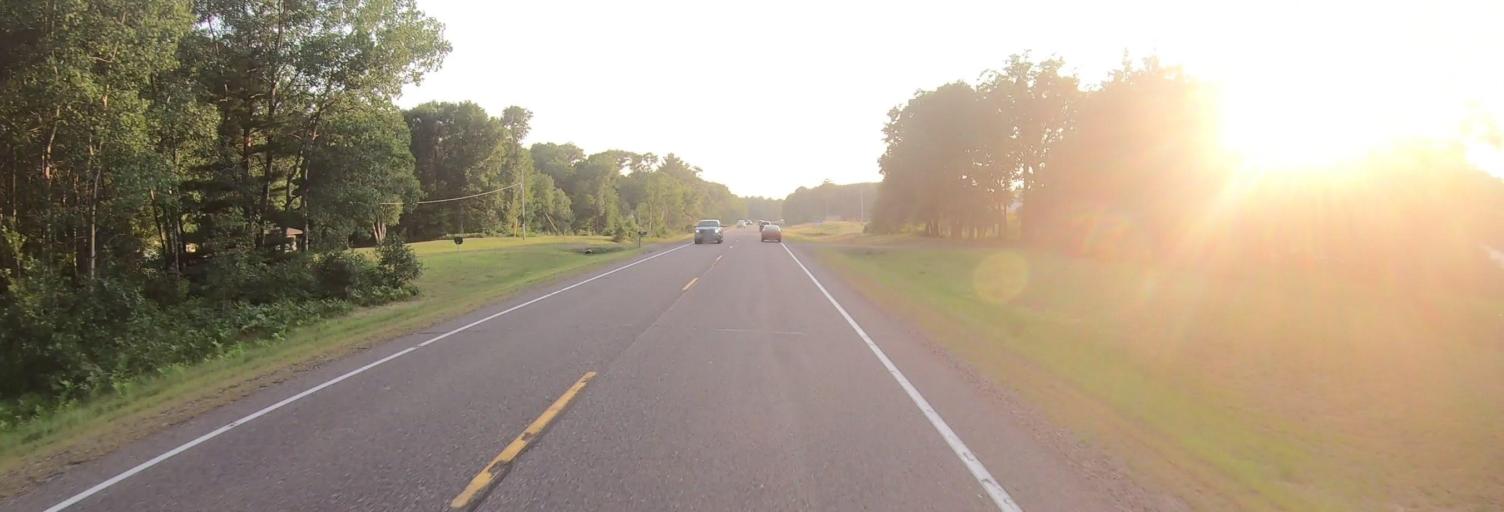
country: US
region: Wisconsin
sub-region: Washburn County
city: Shell Lake
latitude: 45.8112
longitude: -92.1424
